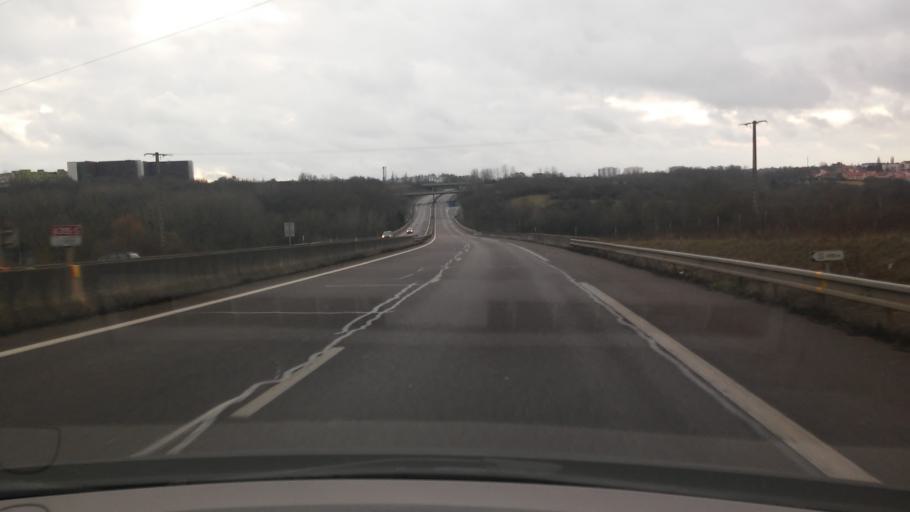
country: FR
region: Lorraine
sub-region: Departement de la Moselle
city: Saint-Julien-les-Metz
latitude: 49.1320
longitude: 6.2441
